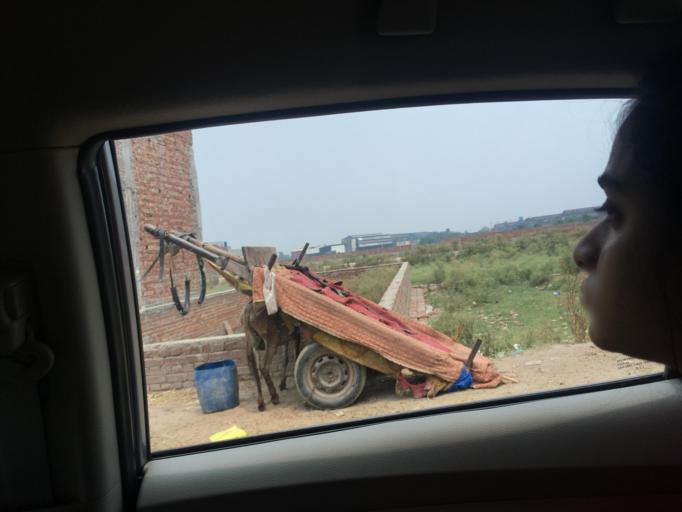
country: PK
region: Punjab
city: Lahore
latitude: 31.6128
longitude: 74.3544
